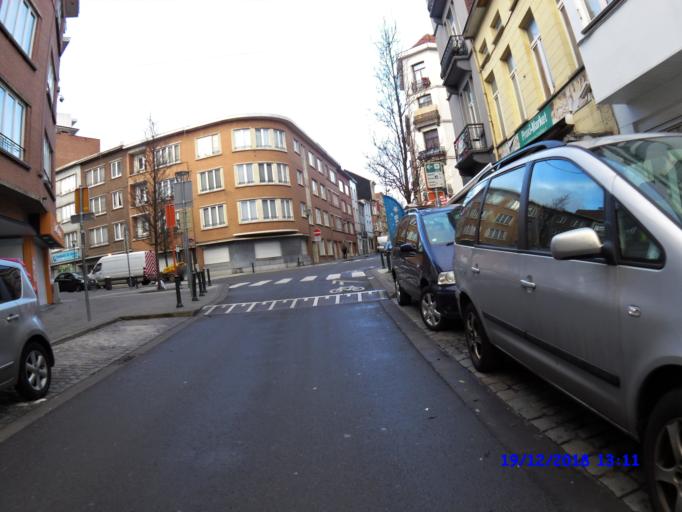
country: BE
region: Brussels Capital
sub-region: Bruxelles-Capitale
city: Brussels
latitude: 50.8594
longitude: 4.3353
